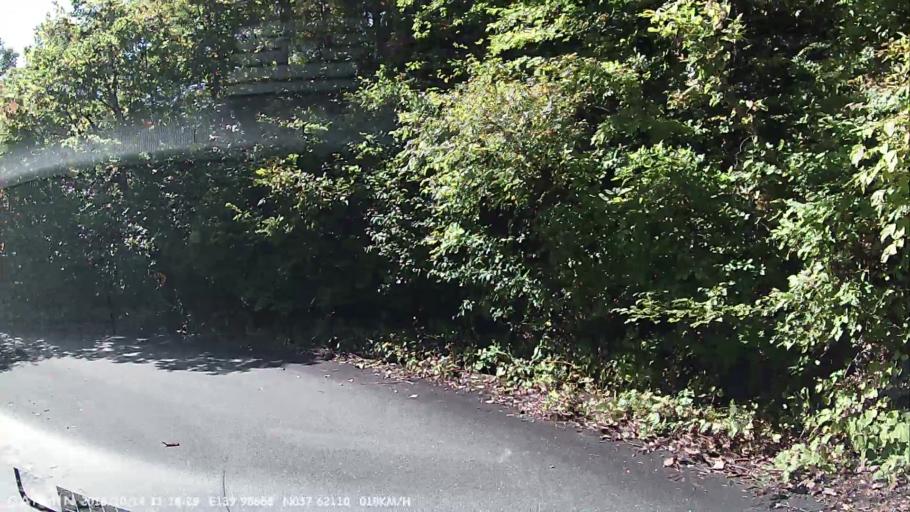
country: JP
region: Fukushima
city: Kitakata
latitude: 37.6211
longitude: 139.9866
